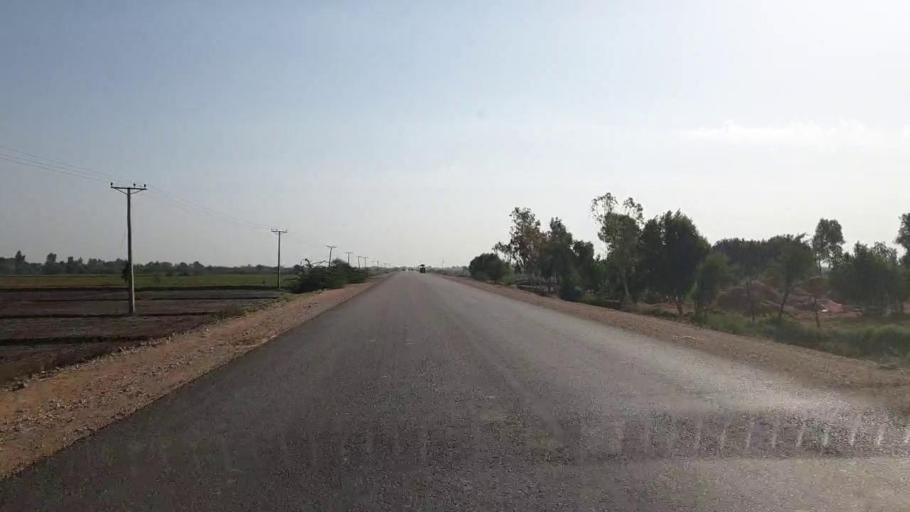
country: PK
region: Sindh
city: Tando Bago
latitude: 24.6570
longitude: 69.0111
